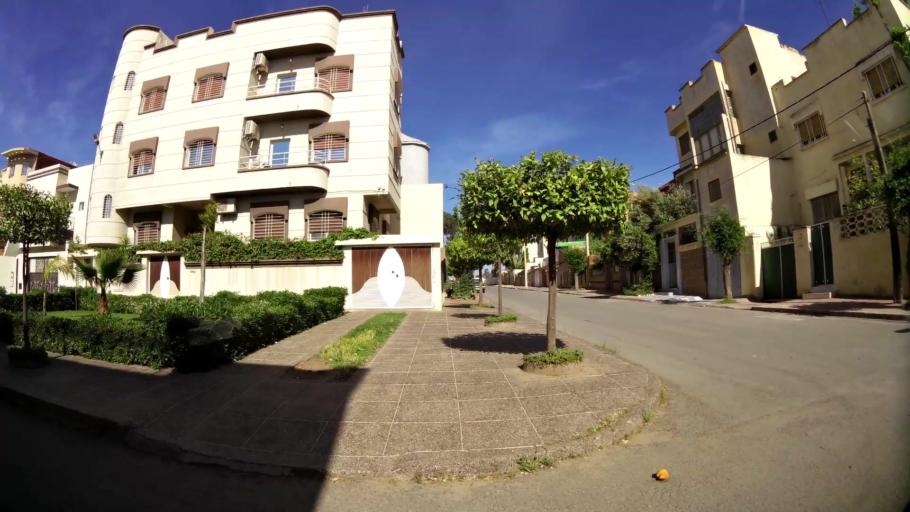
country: MA
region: Oriental
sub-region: Oujda-Angad
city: Oujda
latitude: 34.6699
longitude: -1.9162
